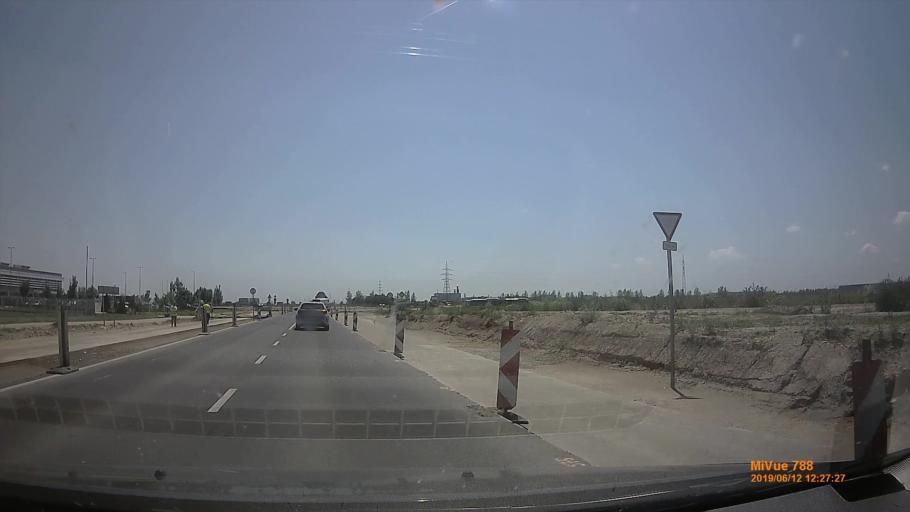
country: HU
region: Bacs-Kiskun
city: Kecskemet
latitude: 46.8802
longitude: 19.7091
